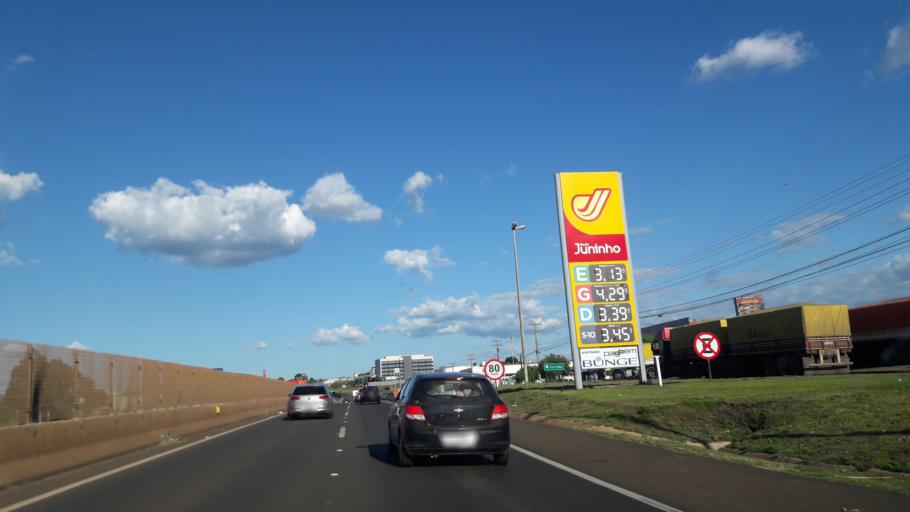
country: BR
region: Parana
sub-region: Guarapuava
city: Guarapuava
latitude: -25.3658
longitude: -51.4831
